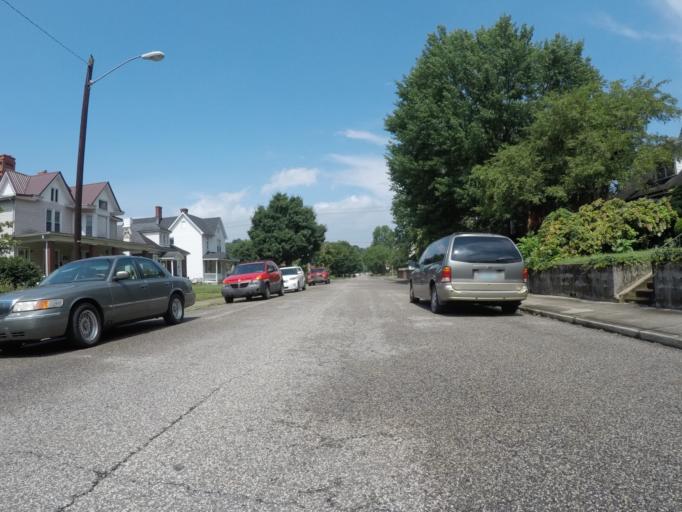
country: US
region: Kentucky
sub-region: Boyd County
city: Ashland
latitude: 38.4752
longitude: -82.6430
